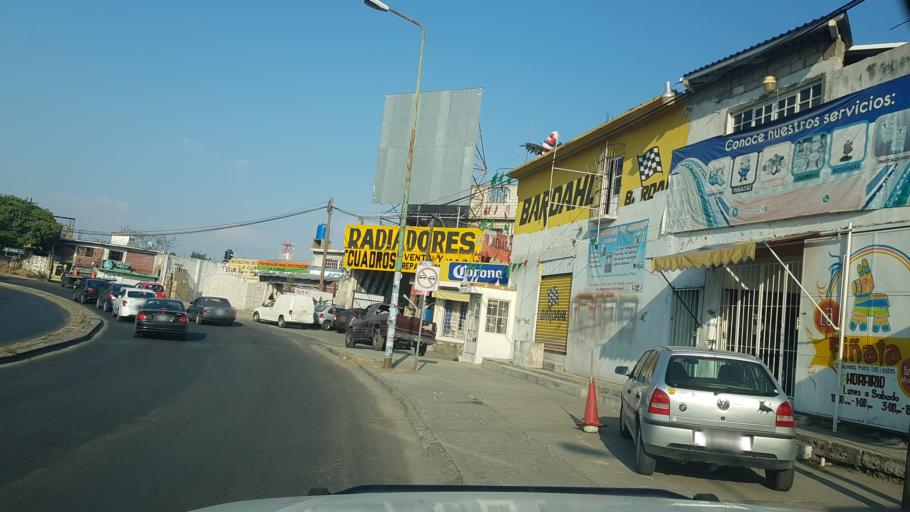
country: MX
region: Puebla
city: Izucar de Matamoros
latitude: 18.6014
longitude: -98.4712
